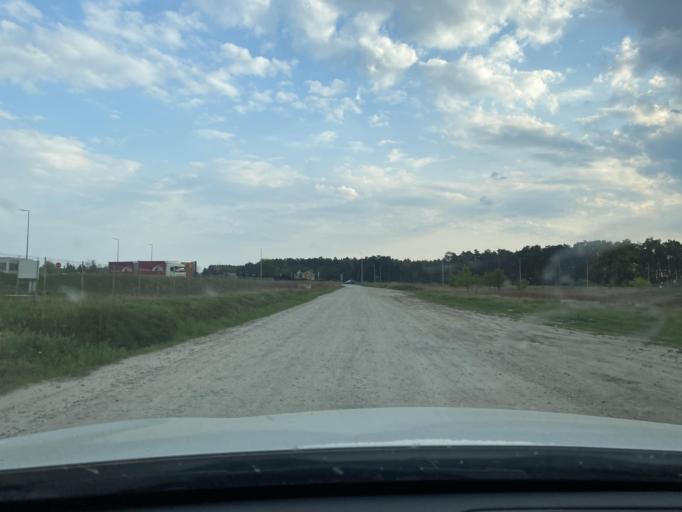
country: PL
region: Lower Silesian Voivodeship
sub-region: Powiat wroclawski
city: Mirkow
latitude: 51.1550
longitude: 17.1571
